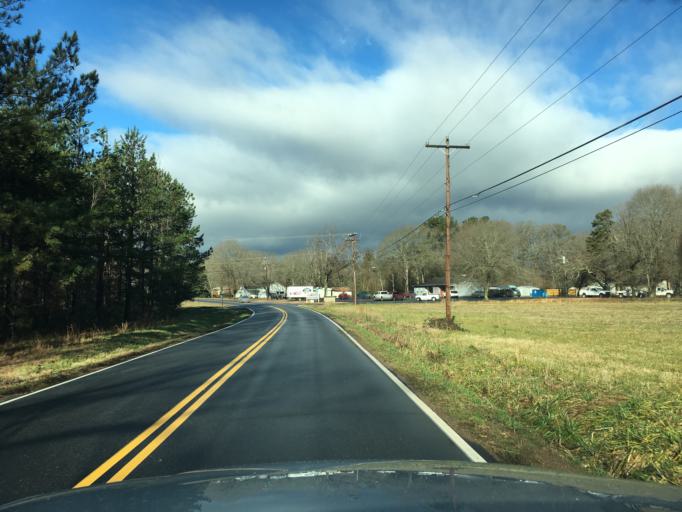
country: US
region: South Carolina
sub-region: Spartanburg County
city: Cowpens
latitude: 35.0148
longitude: -81.8666
